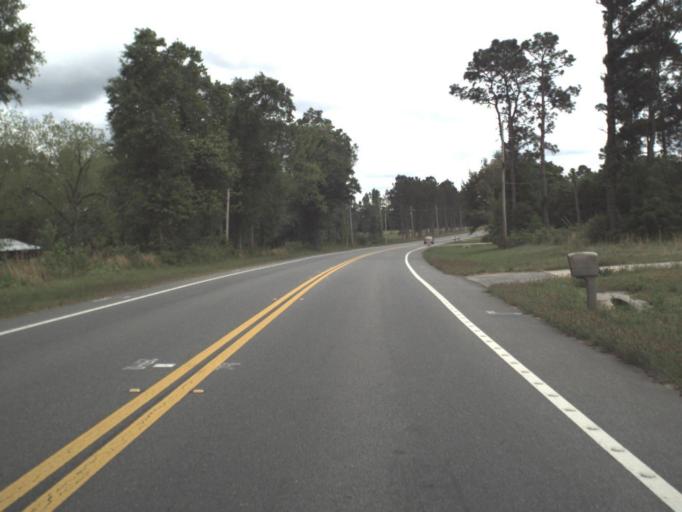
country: US
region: Alabama
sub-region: Escambia County
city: East Brewton
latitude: 30.9335
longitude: -87.0228
